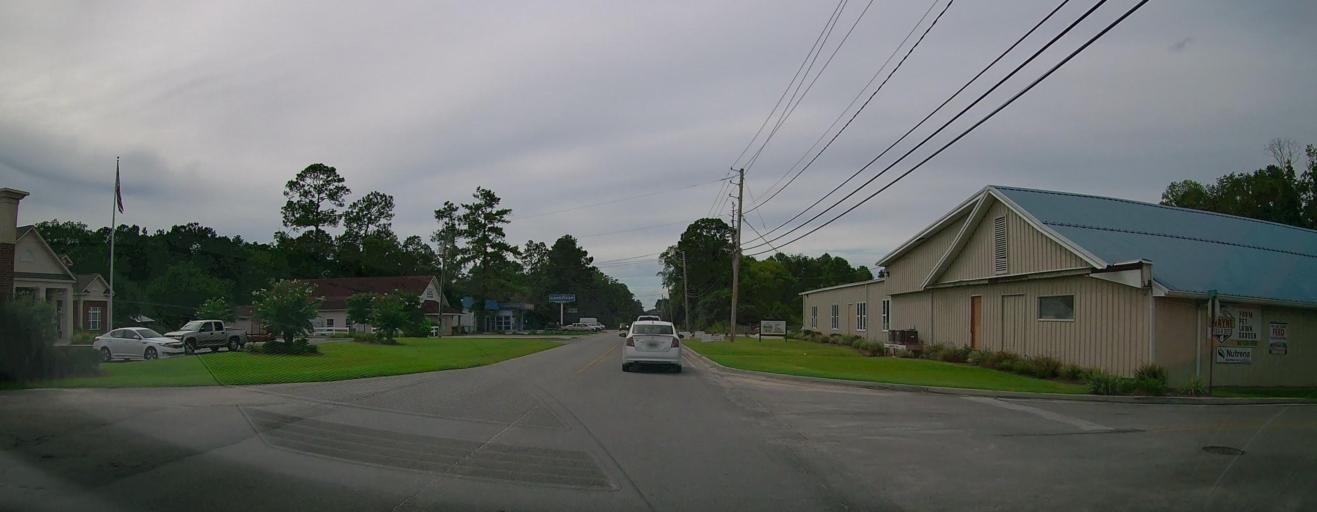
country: US
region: Georgia
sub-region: Wayne County
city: Jesup
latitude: 31.6107
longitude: -81.8895
